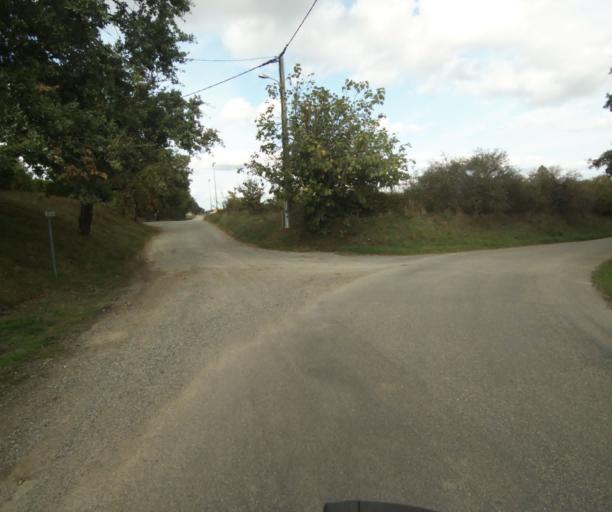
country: FR
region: Midi-Pyrenees
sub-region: Departement du Tarn-et-Garonne
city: Verdun-sur-Garonne
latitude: 43.8418
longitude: 1.1217
